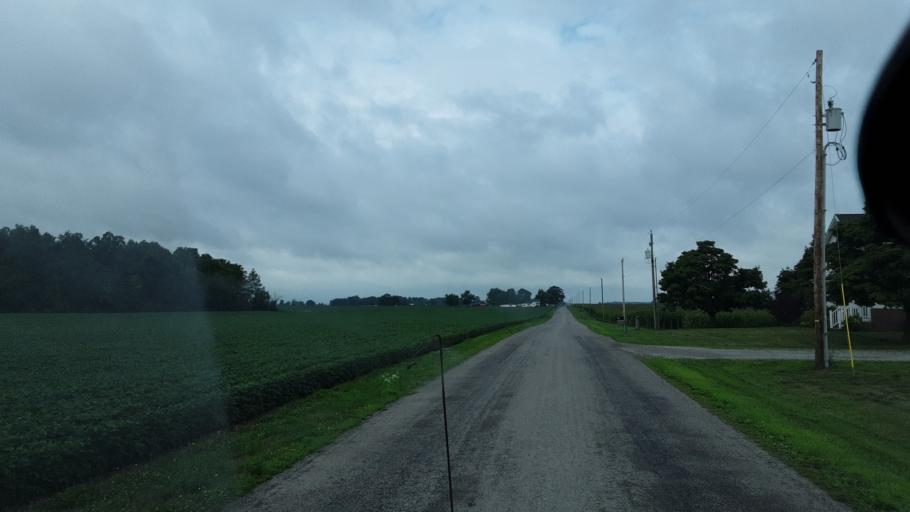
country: US
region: Indiana
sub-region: Allen County
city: Monroeville
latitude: 40.9214
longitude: -84.8487
